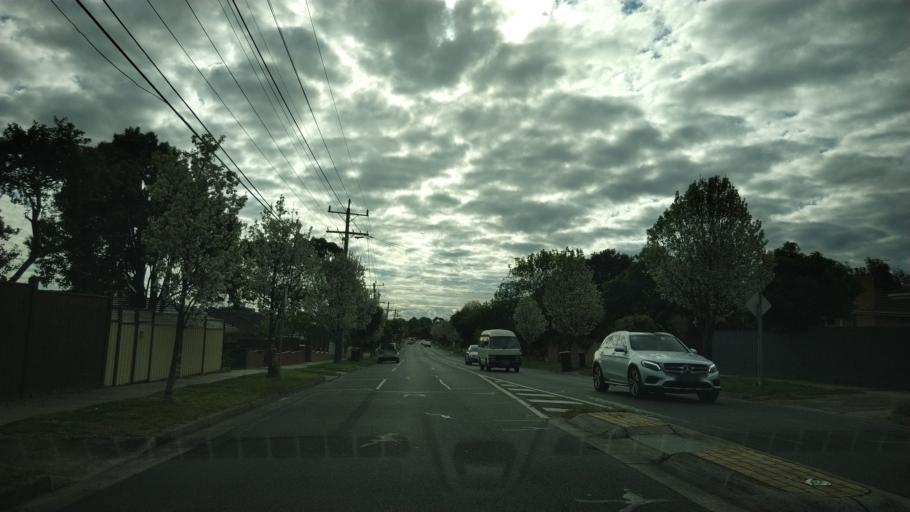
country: AU
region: Victoria
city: Highett
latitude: -37.9533
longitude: 145.0623
